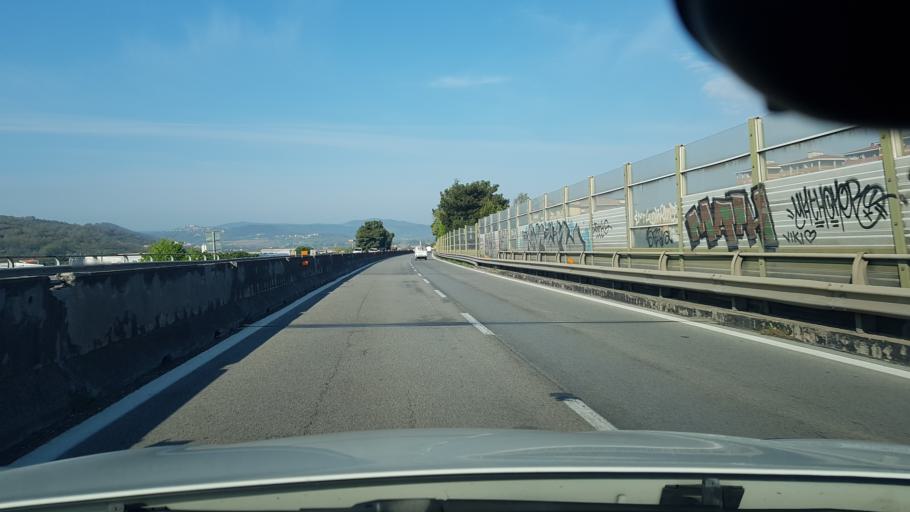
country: IT
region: Umbria
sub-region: Provincia di Perugia
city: Chiugiana-La Commenda
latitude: 43.1024
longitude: 12.3177
